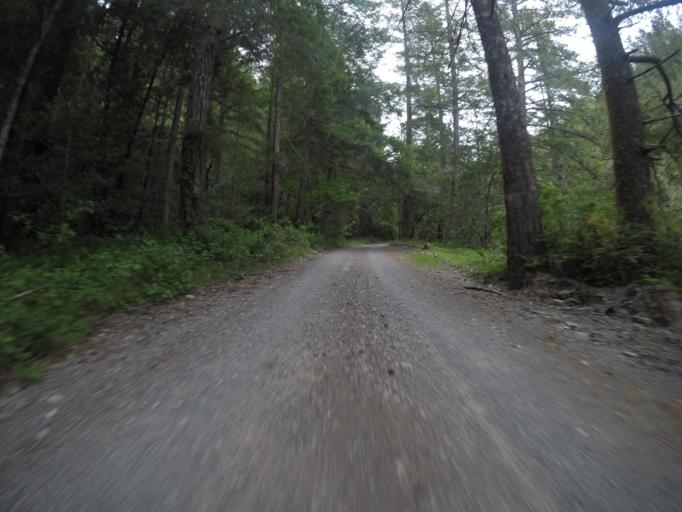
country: US
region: California
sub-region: Del Norte County
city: Bertsch-Oceanview
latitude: 41.7322
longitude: -123.8857
